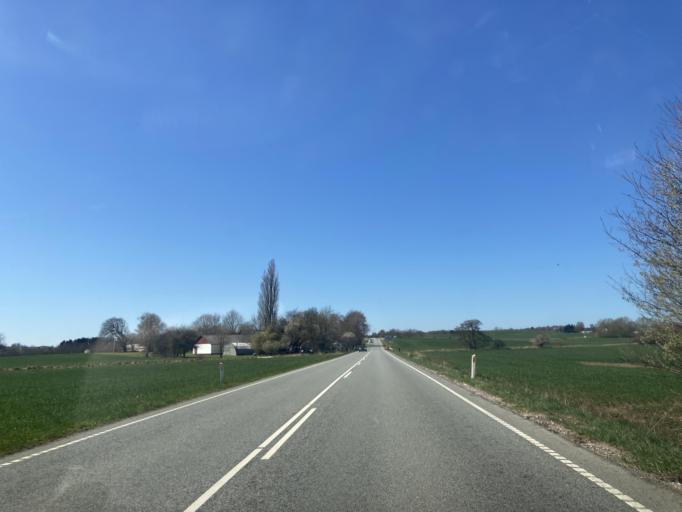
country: DK
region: Capital Region
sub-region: Gribskov Kommune
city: Helsinge
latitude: 56.0049
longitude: 12.2481
